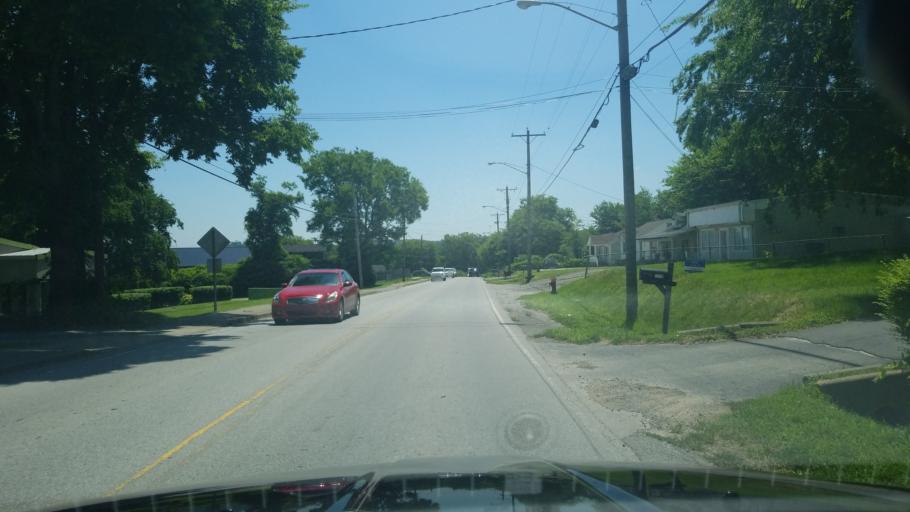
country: US
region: Tennessee
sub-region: Davidson County
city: Belle Meade
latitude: 36.1564
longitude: -86.8651
